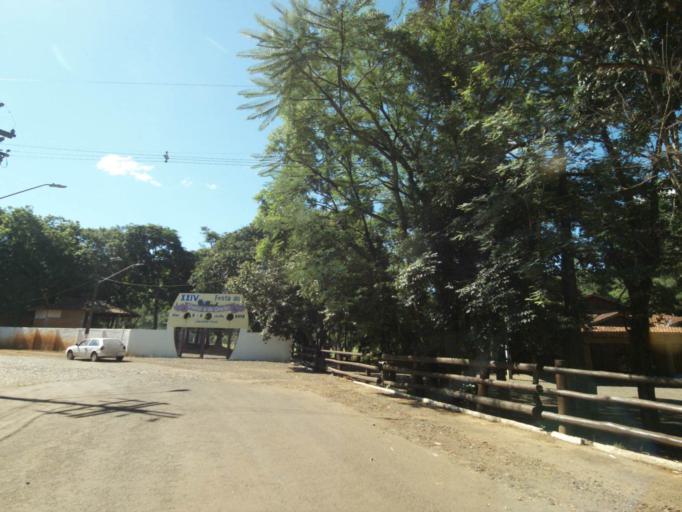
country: BR
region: Parana
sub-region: Ampere
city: Ampere
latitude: -26.1682
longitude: -53.3638
